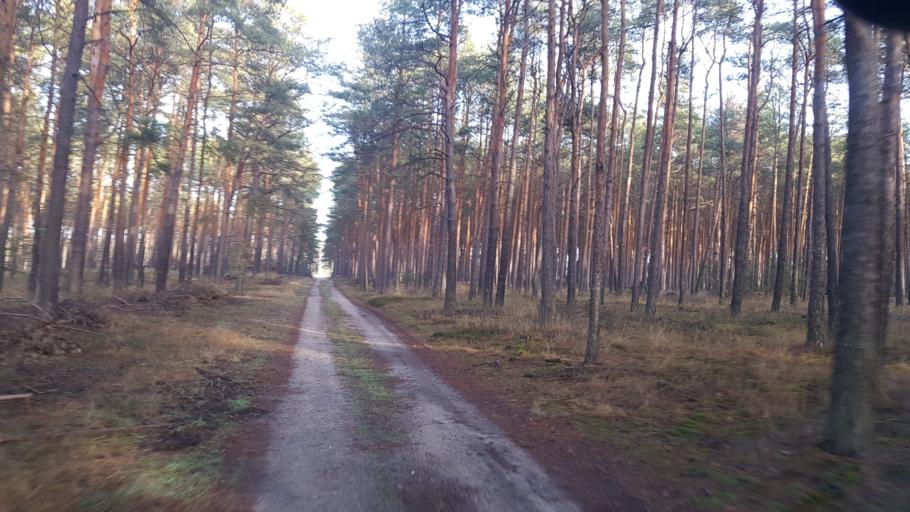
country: DE
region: Brandenburg
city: Schilda
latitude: 51.6351
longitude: 13.3967
